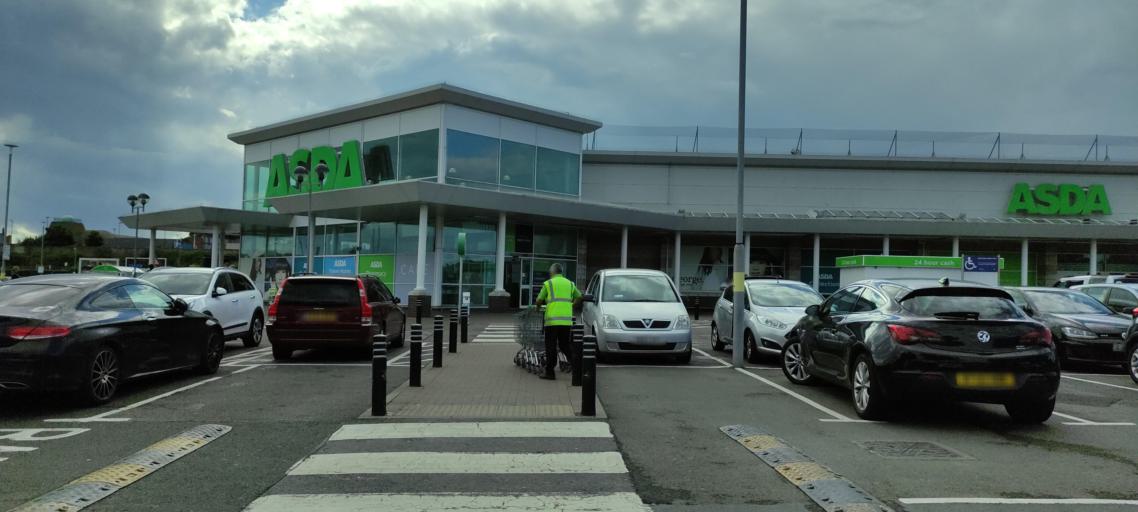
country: GB
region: England
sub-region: Hartlepool
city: Hartlepool
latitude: 54.6892
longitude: -1.2090
